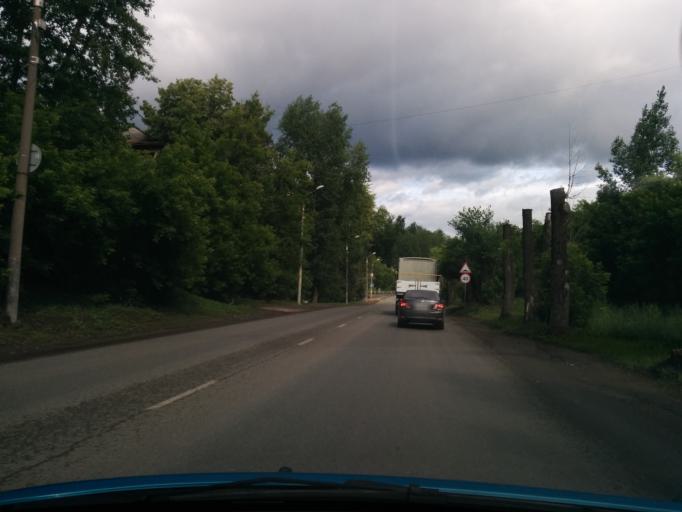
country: RU
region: Perm
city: Kondratovo
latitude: 58.0449
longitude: 56.0900
